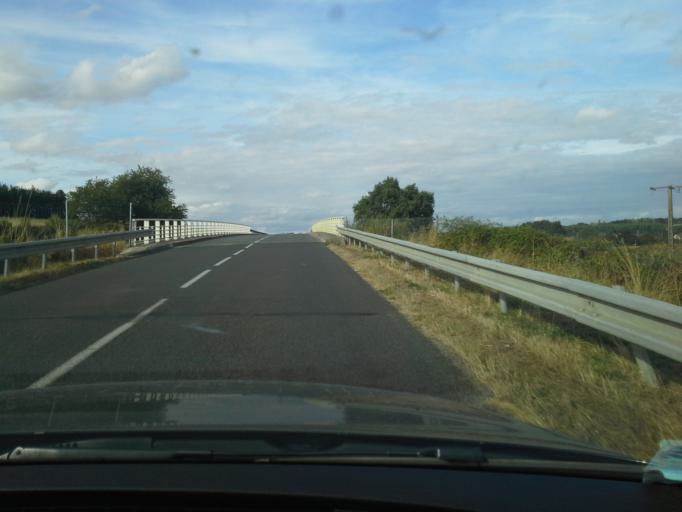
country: FR
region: Centre
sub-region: Departement d'Indre-et-Loire
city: Auzouer-en-Touraine
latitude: 47.5164
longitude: 0.9122
